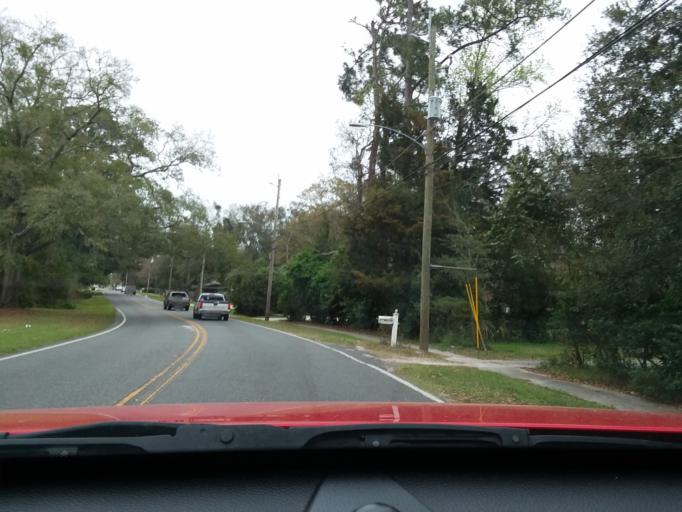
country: US
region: Florida
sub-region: Duval County
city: Jacksonville
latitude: 30.2945
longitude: -81.7484
